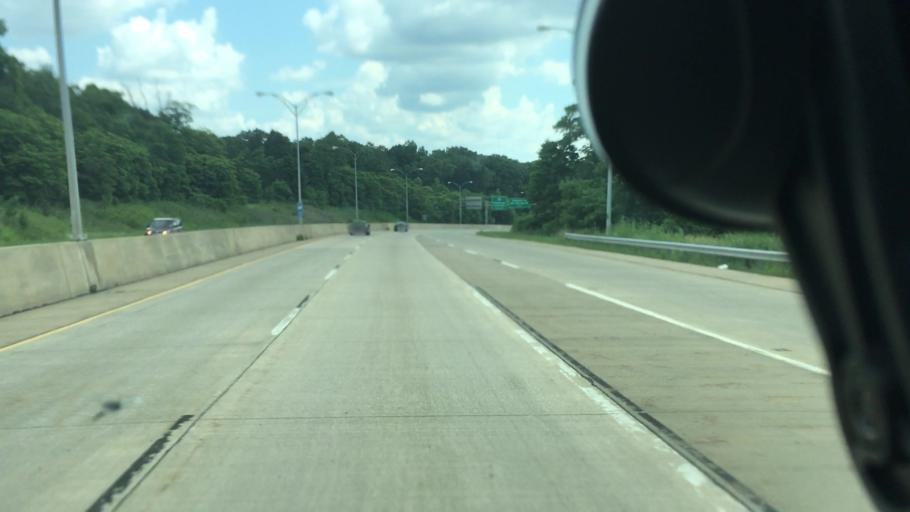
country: US
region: Ohio
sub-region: Trumbull County
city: Churchill
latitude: 41.1297
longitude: -80.6748
